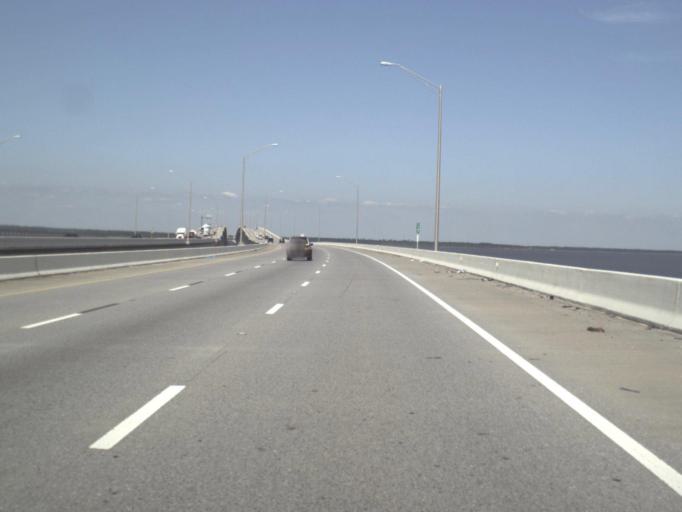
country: US
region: Florida
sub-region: Escambia County
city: Ferry Pass
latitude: 30.5098
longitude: -87.1571
